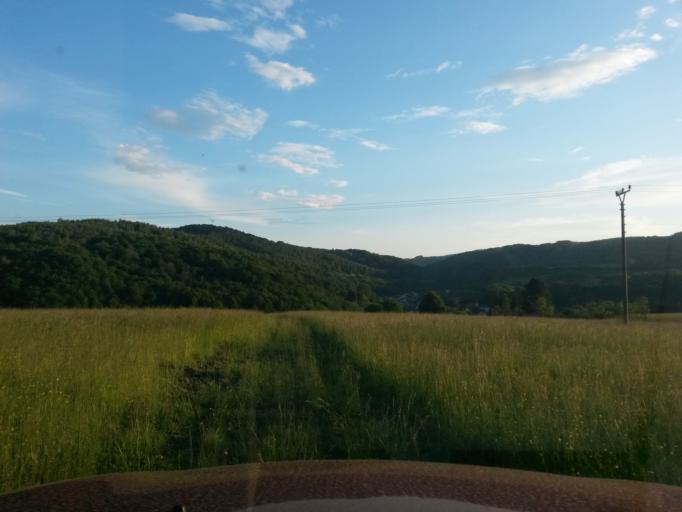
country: UA
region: Zakarpattia
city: Velykyi Bereznyi
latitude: 48.8589
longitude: 22.3619
